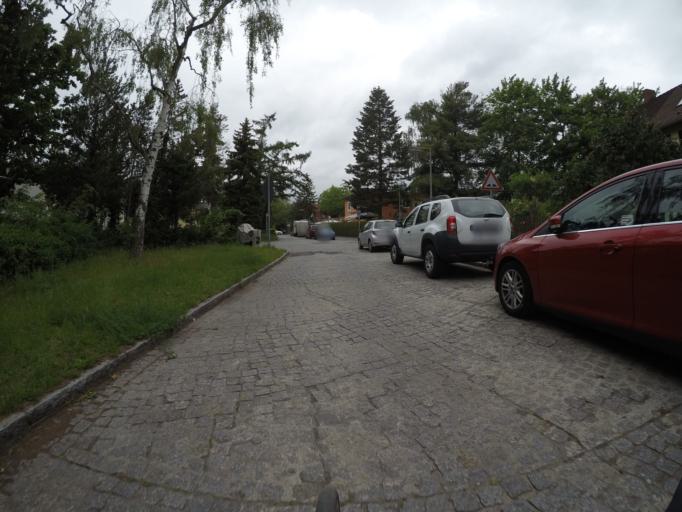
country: DE
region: Berlin
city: Tegel
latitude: 52.5965
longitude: 13.2962
